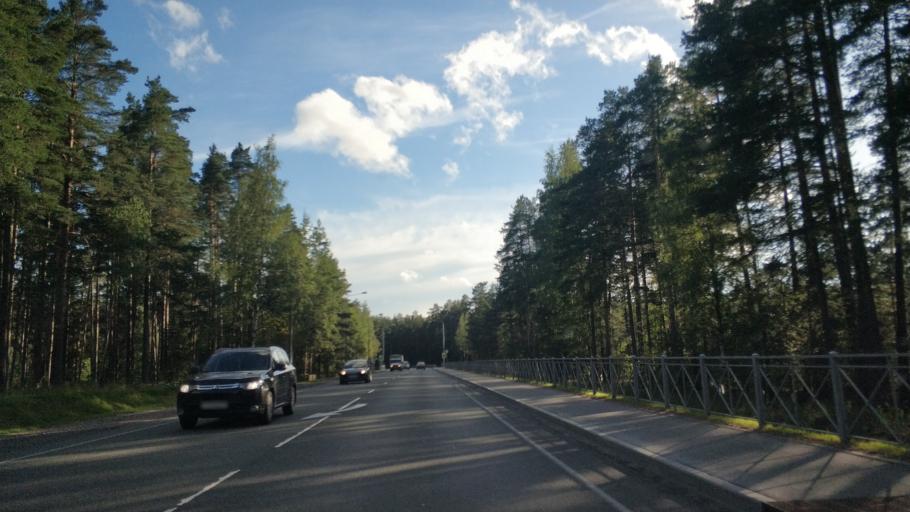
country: RU
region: Leningrad
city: Sapernoye
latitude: 60.7096
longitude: 29.9718
